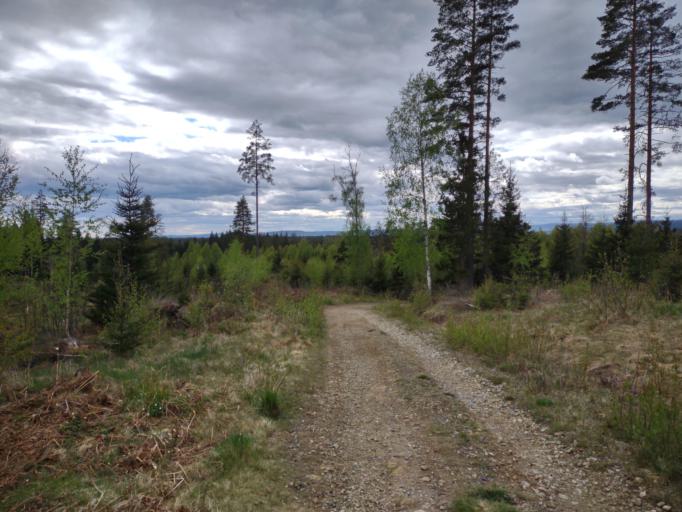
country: NO
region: Akershus
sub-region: Eidsvoll
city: Raholt
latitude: 60.2738
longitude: 11.1494
